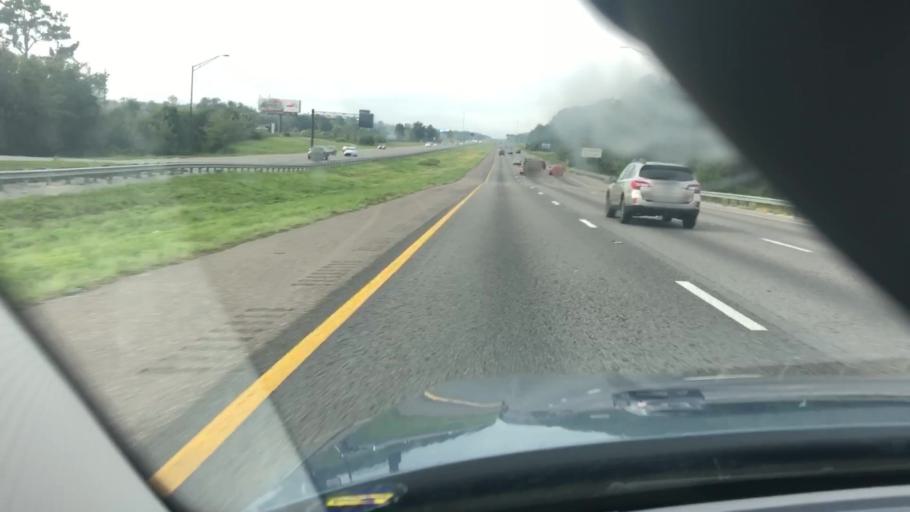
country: US
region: Florida
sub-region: Polk County
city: Loughman
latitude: 28.2760
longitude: -81.5992
